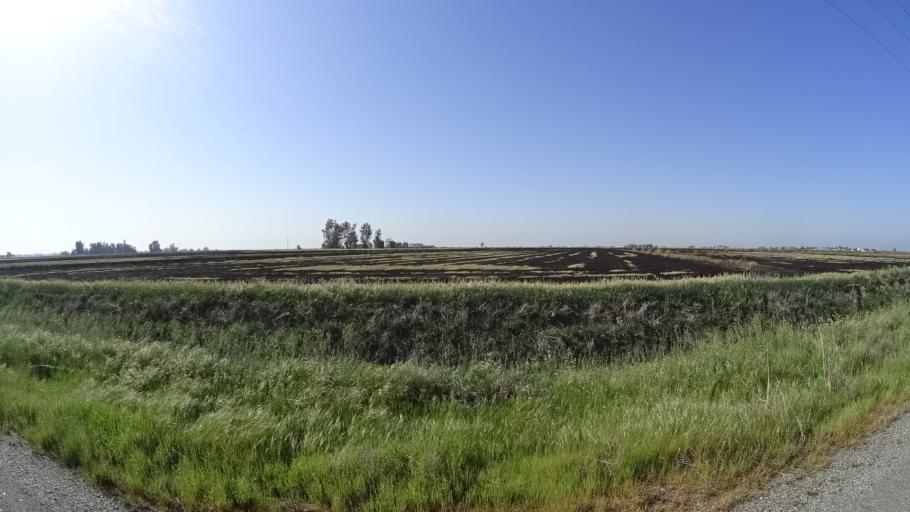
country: US
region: California
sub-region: Glenn County
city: Willows
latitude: 39.6016
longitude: -122.0684
